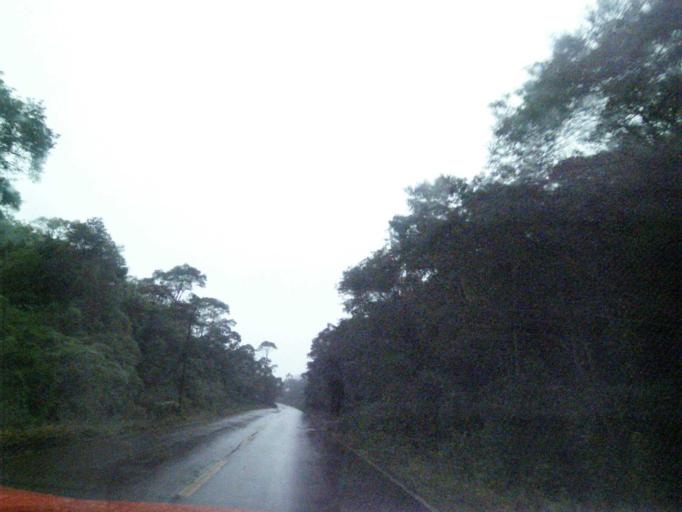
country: BR
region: Santa Catarina
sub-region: Anitapolis
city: Anitapolis
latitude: -27.7746
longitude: -49.0412
